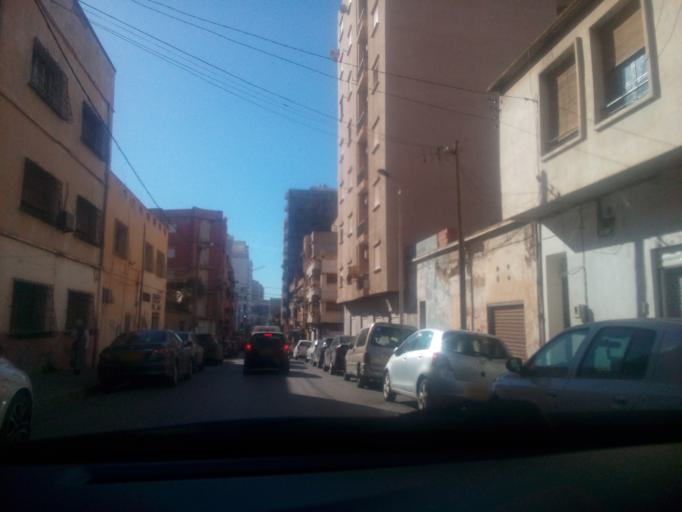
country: DZ
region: Oran
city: Oran
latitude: 35.7107
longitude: -0.6202
